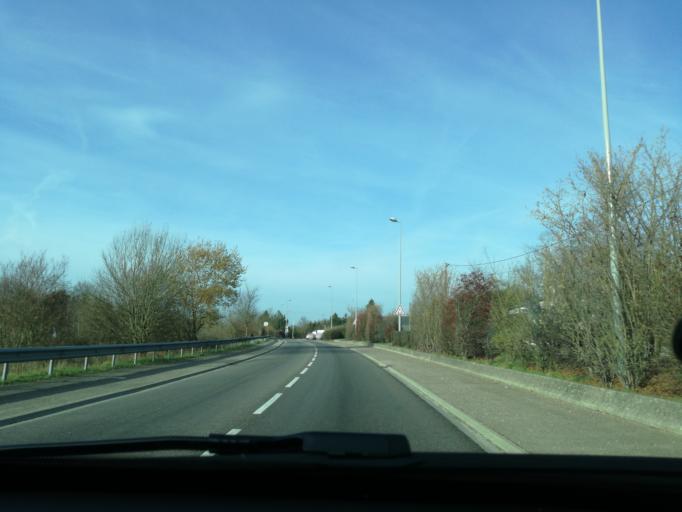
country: FR
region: Lorraine
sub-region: Departement de la Meuse
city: Bar-le-Duc
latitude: 48.7858
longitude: 5.1516
